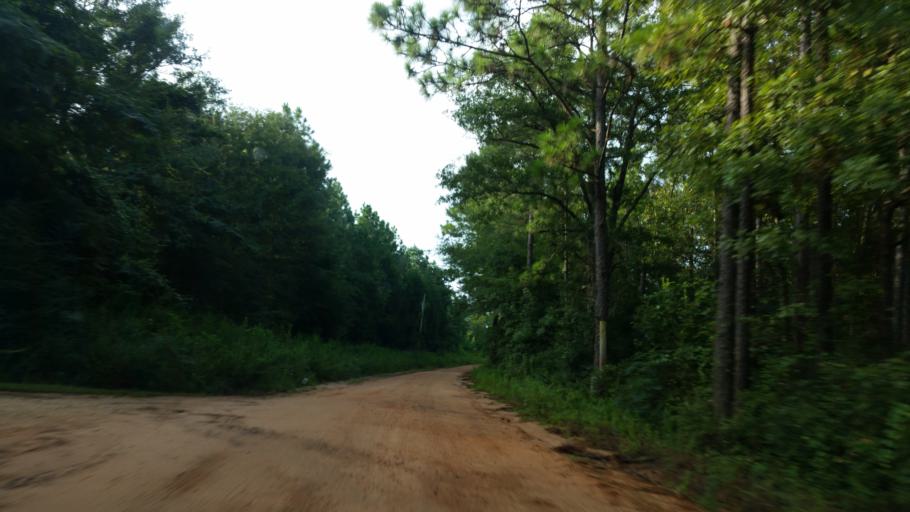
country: US
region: Alabama
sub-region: Escambia County
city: Atmore
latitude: 30.8553
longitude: -87.5770
